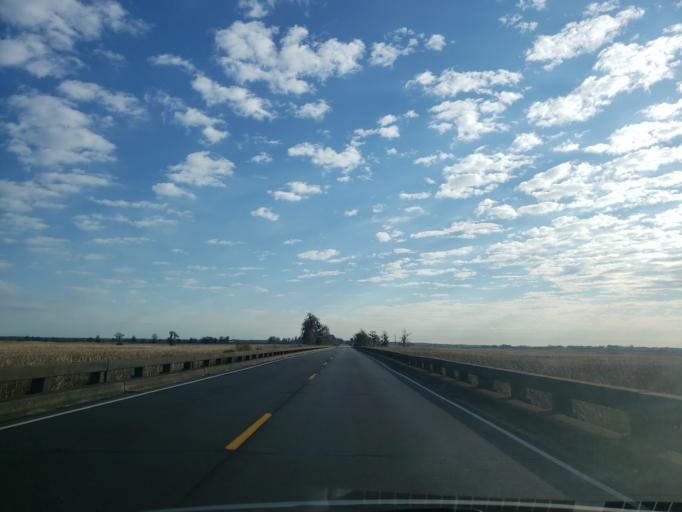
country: US
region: Georgia
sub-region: Chatham County
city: Port Wentworth
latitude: 32.1658
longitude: -81.1364
